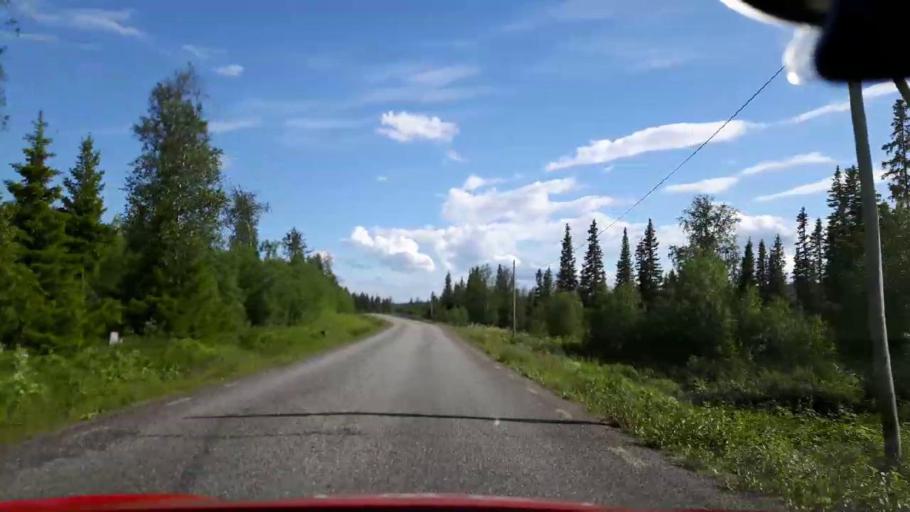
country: SE
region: Jaemtland
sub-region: Krokoms Kommun
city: Valla
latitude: 63.7089
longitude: 14.1417
